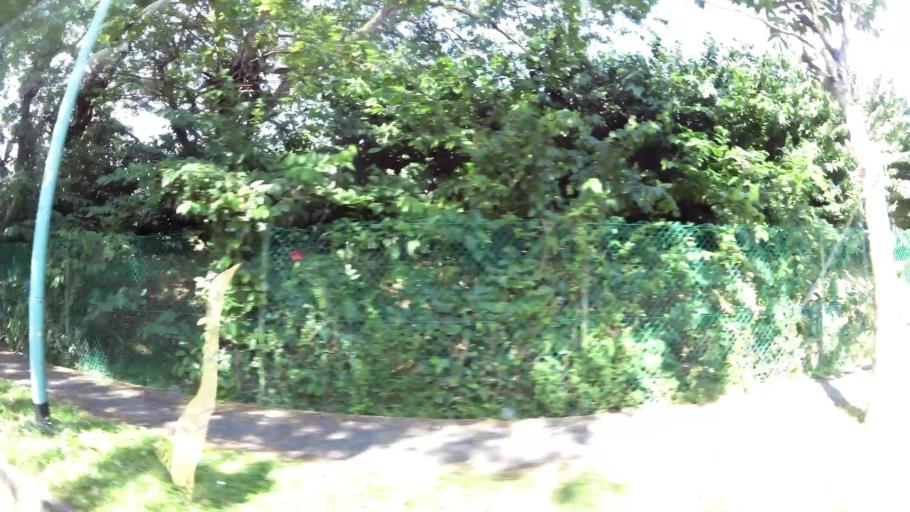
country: SG
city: Singapore
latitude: 1.3738
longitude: 103.8295
